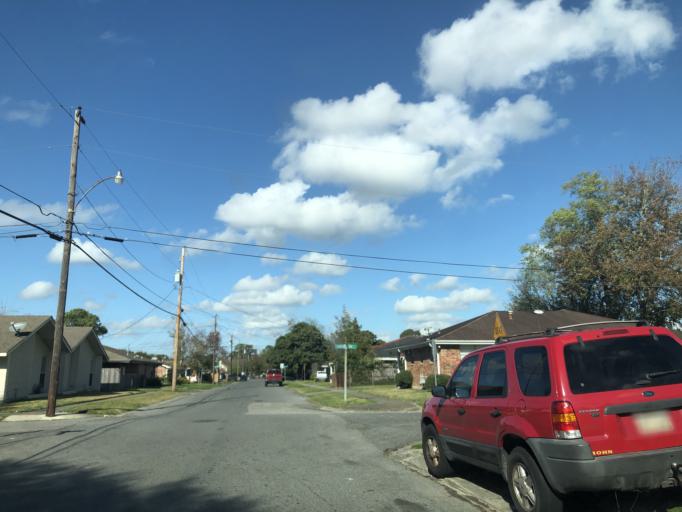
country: US
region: Louisiana
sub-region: Jefferson Parish
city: Metairie Terrace
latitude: 29.9831
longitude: -90.1630
